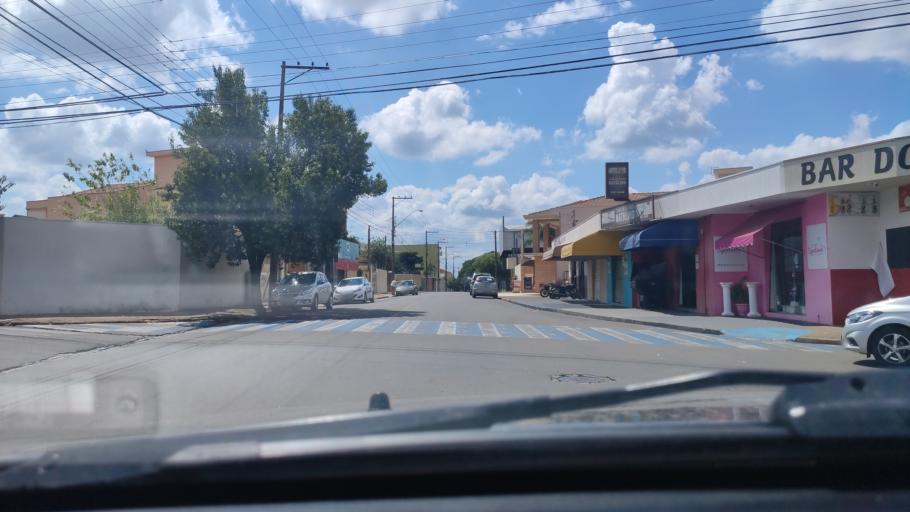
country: BR
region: Sao Paulo
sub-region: Sao Carlos
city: Sao Carlos
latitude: -22.0000
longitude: -47.8792
